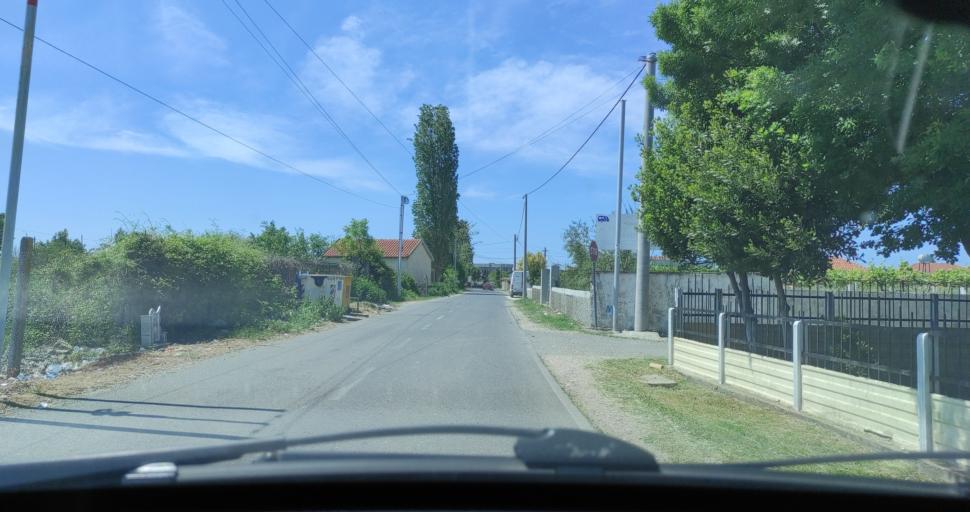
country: AL
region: Lezhe
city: Lezhe
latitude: 41.7575
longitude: 19.6244
